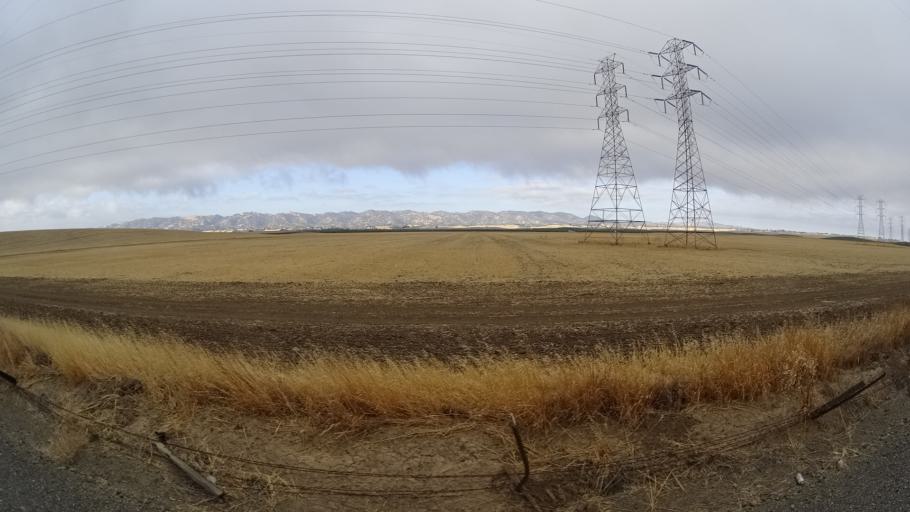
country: US
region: California
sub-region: Yolo County
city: Dunnigan
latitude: 38.8290
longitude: -122.0434
